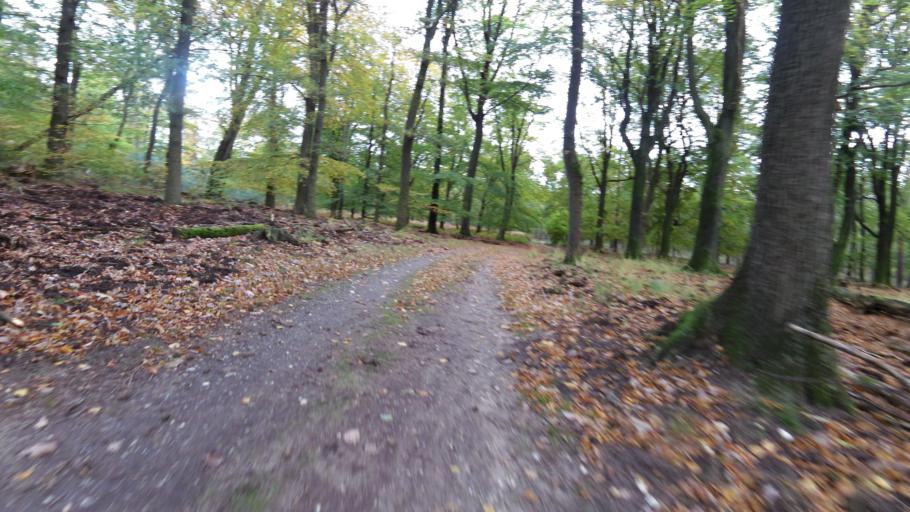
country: NL
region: Gelderland
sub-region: Gemeente Epe
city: Vaassen
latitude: 52.3202
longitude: 5.8706
